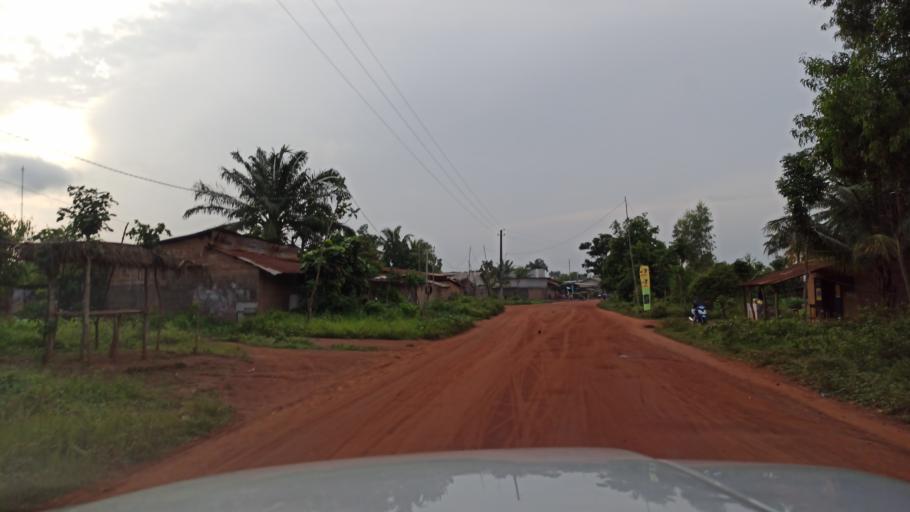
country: BJ
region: Queme
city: Porto-Novo
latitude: 6.5166
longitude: 2.6791
